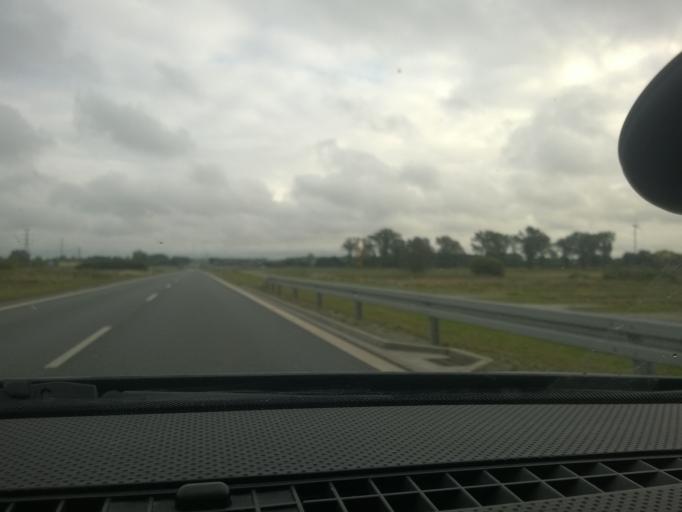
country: PL
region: Lodz Voivodeship
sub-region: Powiat sieradzki
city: Sieradz
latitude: 51.5709
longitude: 18.6974
